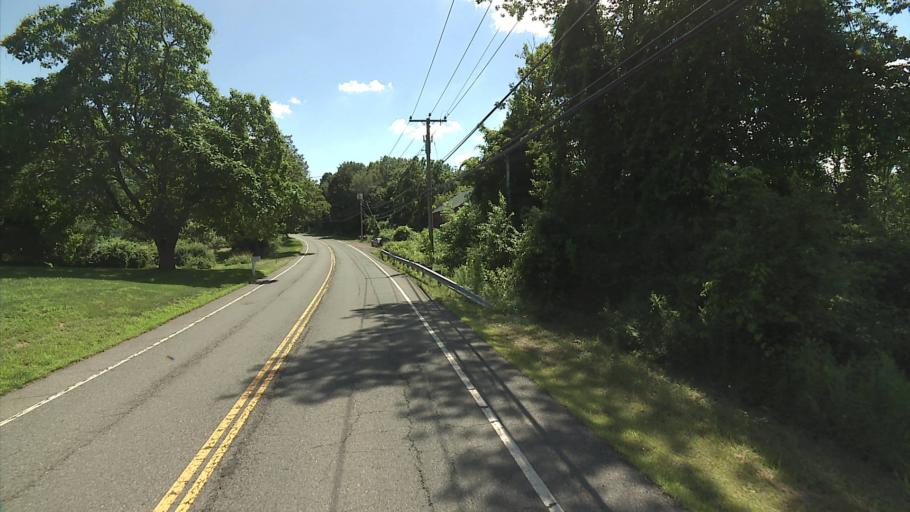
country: US
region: Massachusetts
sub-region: Hampden County
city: Southwick
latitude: 42.0164
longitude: -72.7274
